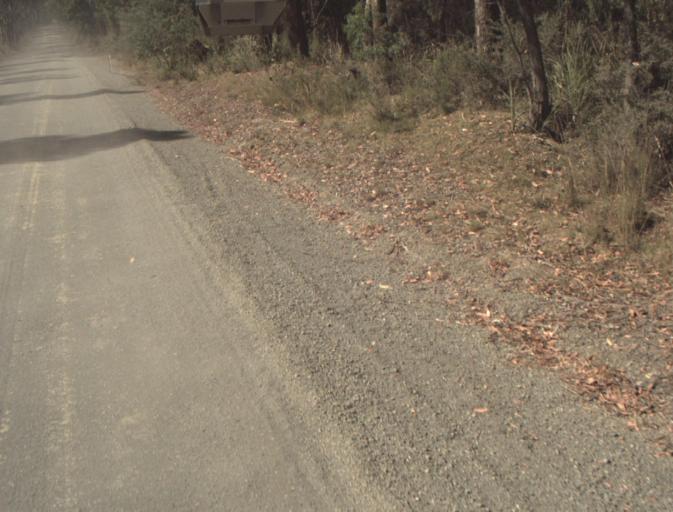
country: AU
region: Tasmania
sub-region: Launceston
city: Mayfield
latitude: -41.3508
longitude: 147.2193
